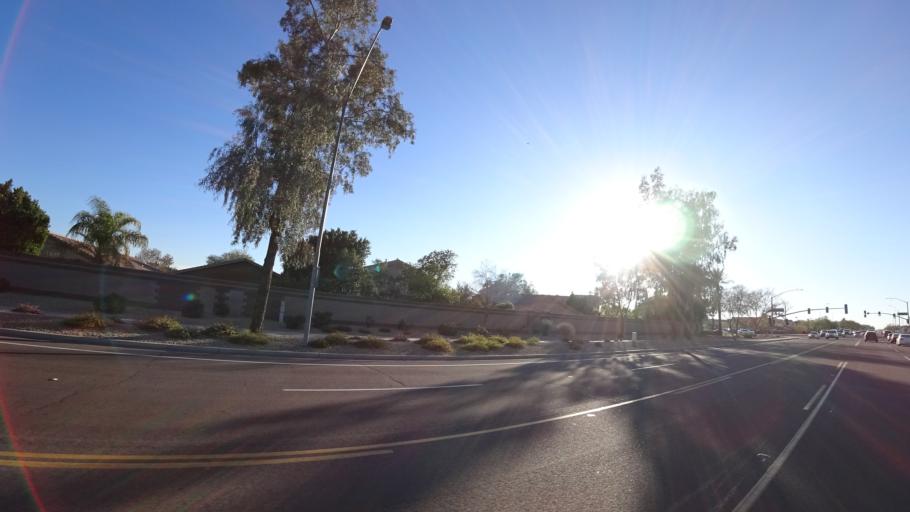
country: US
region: Arizona
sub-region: Maricopa County
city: Sun City
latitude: 33.6816
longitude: -112.2365
